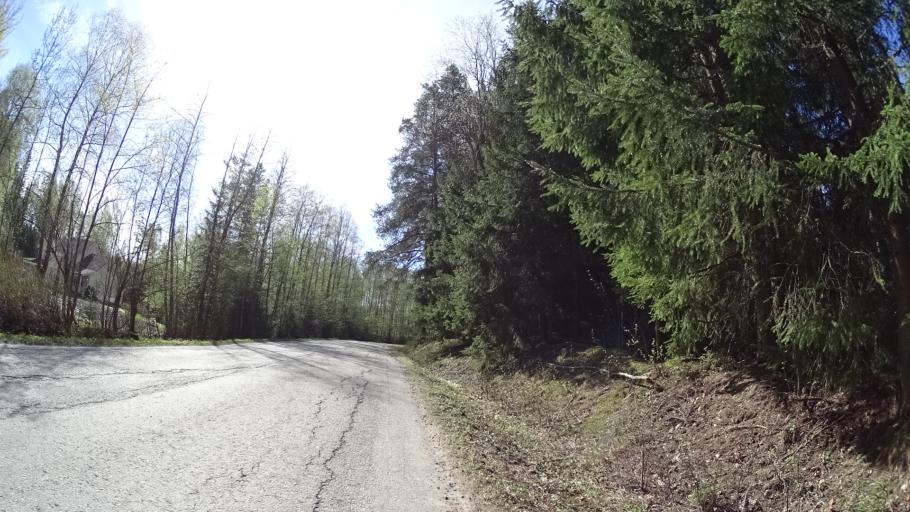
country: FI
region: Uusimaa
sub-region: Helsinki
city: Nurmijaervi
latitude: 60.4536
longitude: 24.8260
